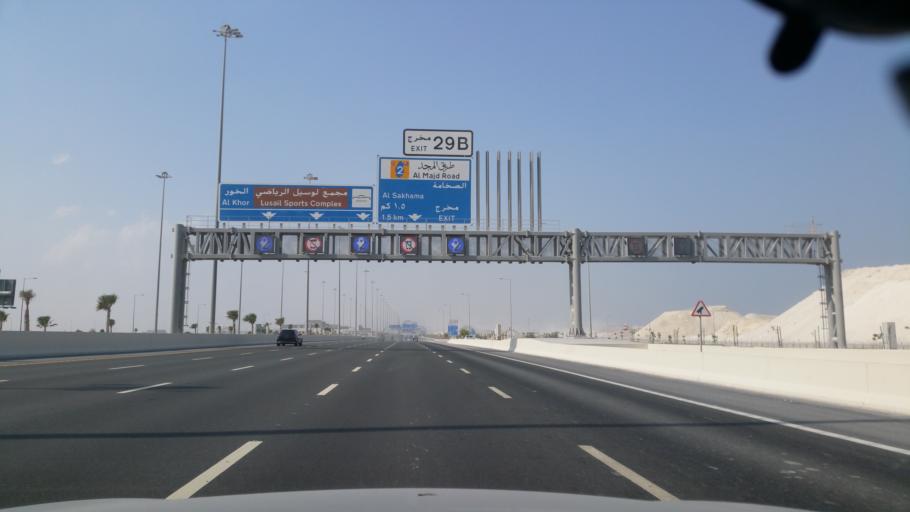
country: QA
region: Baladiyat Umm Salal
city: Umm Salal Muhammad
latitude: 25.4348
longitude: 51.4835
